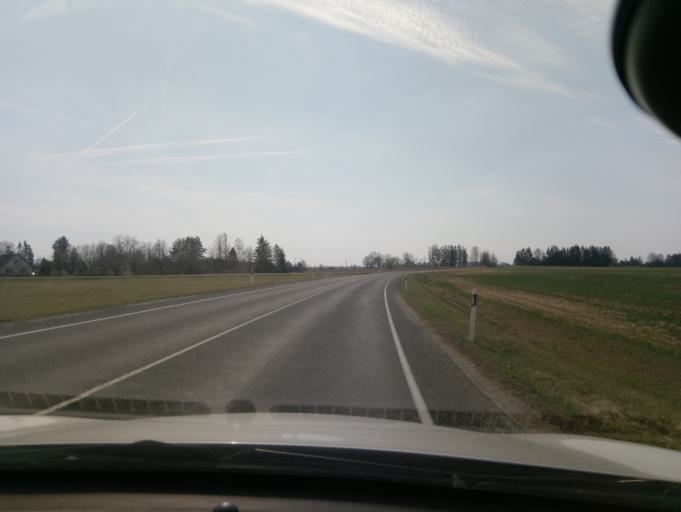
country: EE
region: Viljandimaa
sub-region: Vohma linn
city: Vohma
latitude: 58.6904
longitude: 25.6258
